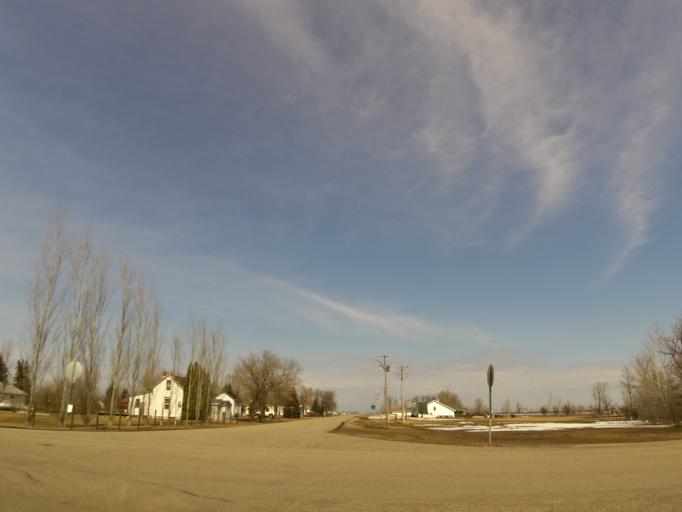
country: US
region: North Dakota
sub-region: Walsh County
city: Grafton
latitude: 48.2953
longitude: -97.2547
